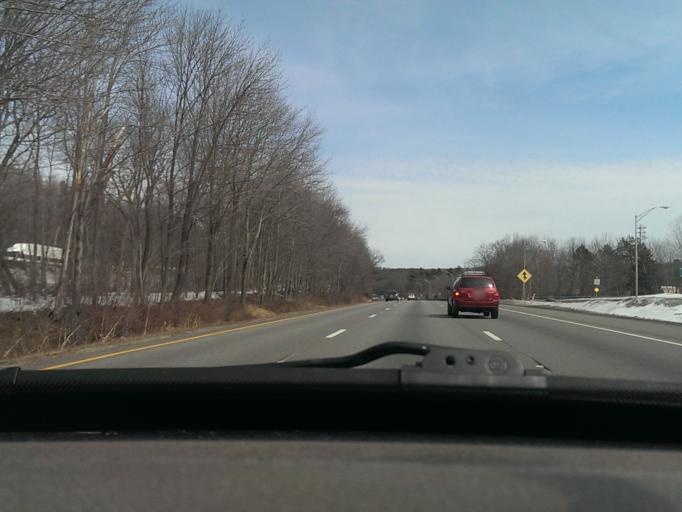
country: US
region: Massachusetts
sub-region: Worcester County
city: Charlton
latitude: 42.1406
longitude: -72.0250
